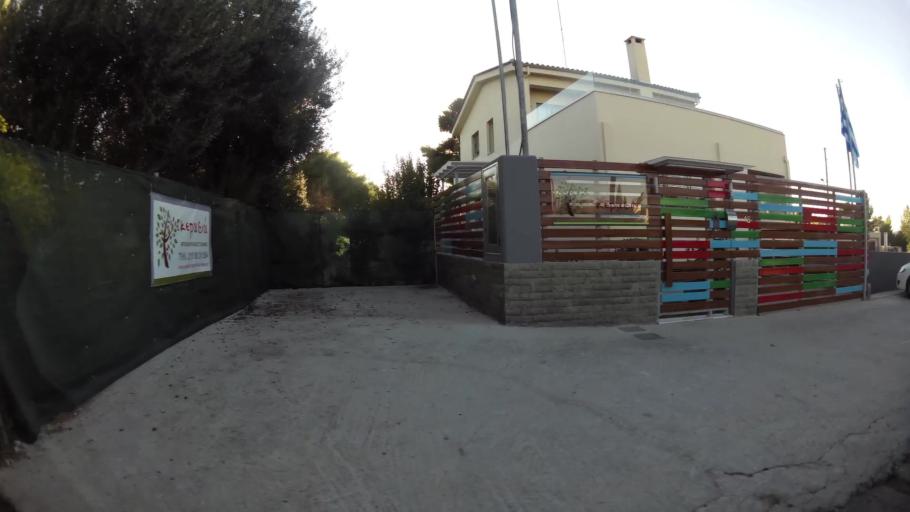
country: GR
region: Attica
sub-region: Nomarchia Anatolikis Attikis
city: Pallini
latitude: 38.0025
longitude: 23.8672
